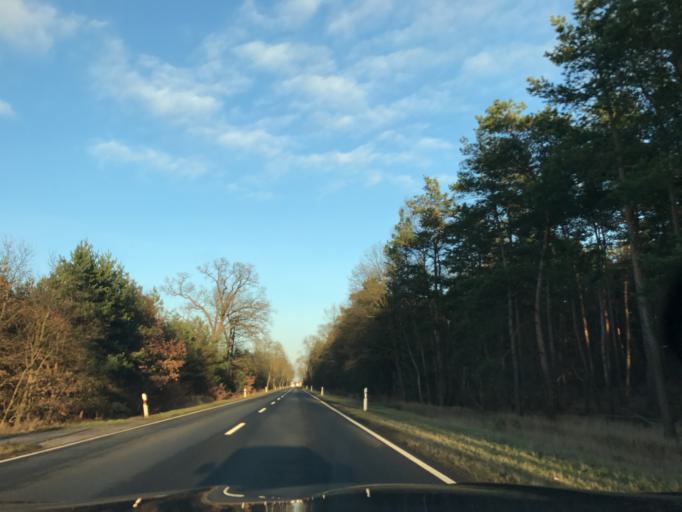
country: DE
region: Saxony-Anhalt
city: Genthin
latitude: 52.3821
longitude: 12.1246
